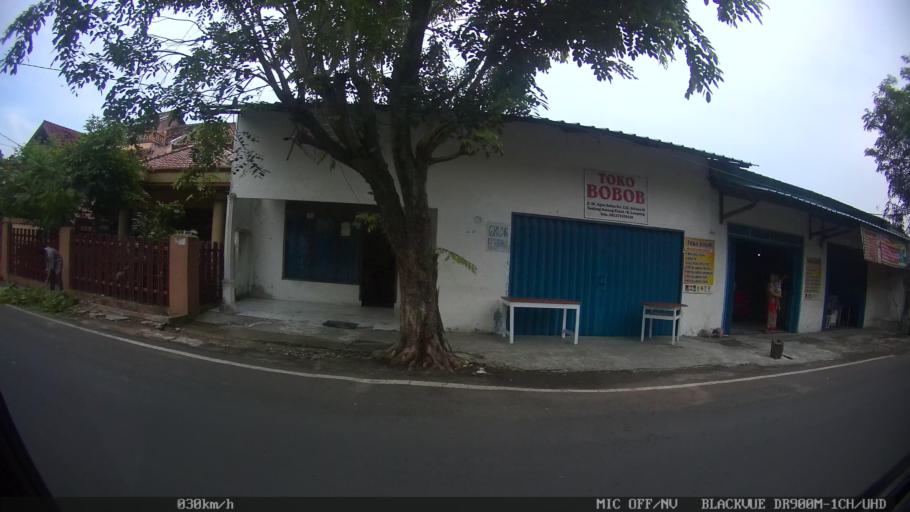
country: ID
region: Lampung
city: Bandarlampung
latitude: -5.4117
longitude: 105.2488
